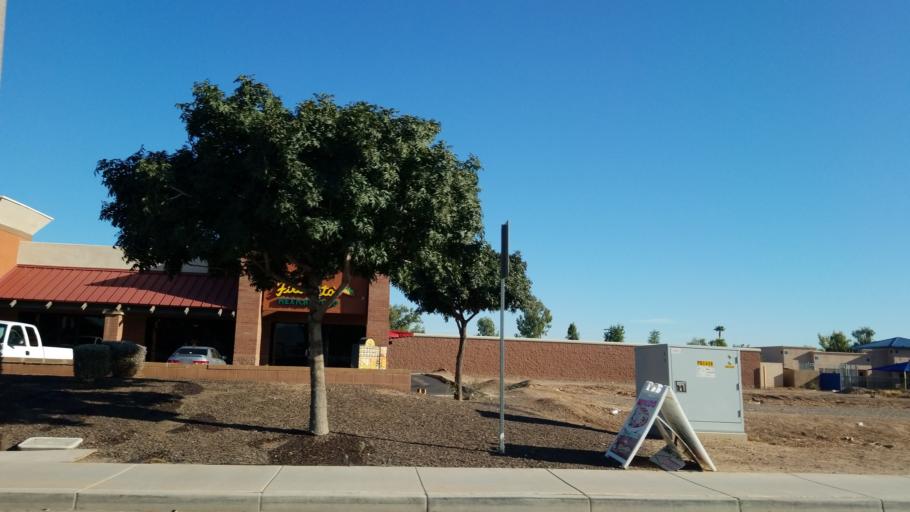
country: US
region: Arizona
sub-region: Maricopa County
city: Tolleson
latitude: 33.4503
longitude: -112.2673
